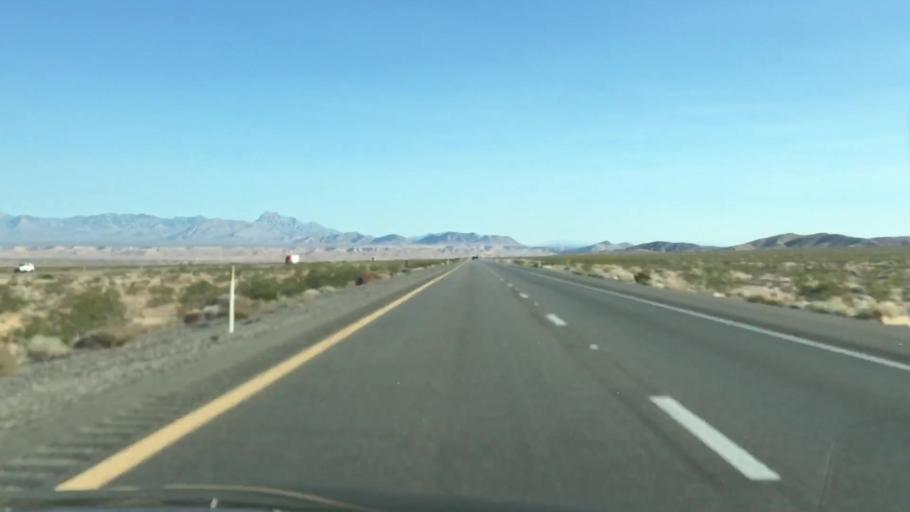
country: US
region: Nevada
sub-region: Clark County
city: Moapa Town
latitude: 36.6176
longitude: -114.6206
